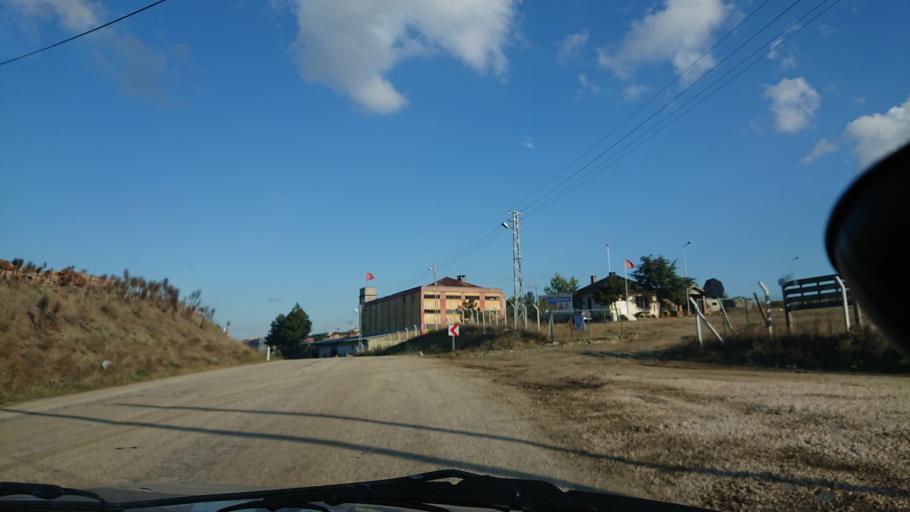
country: TR
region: Bilecik
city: Pazaryeri
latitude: 39.9999
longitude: 29.8873
